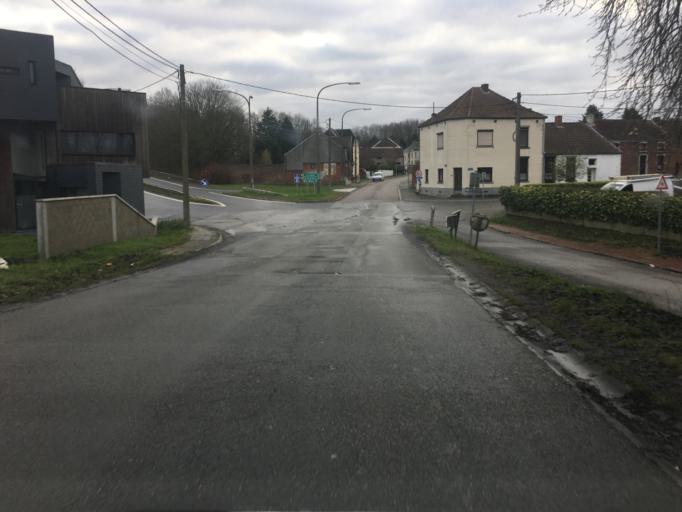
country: BE
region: Wallonia
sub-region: Province du Hainaut
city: Manage
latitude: 50.5084
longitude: 4.2101
